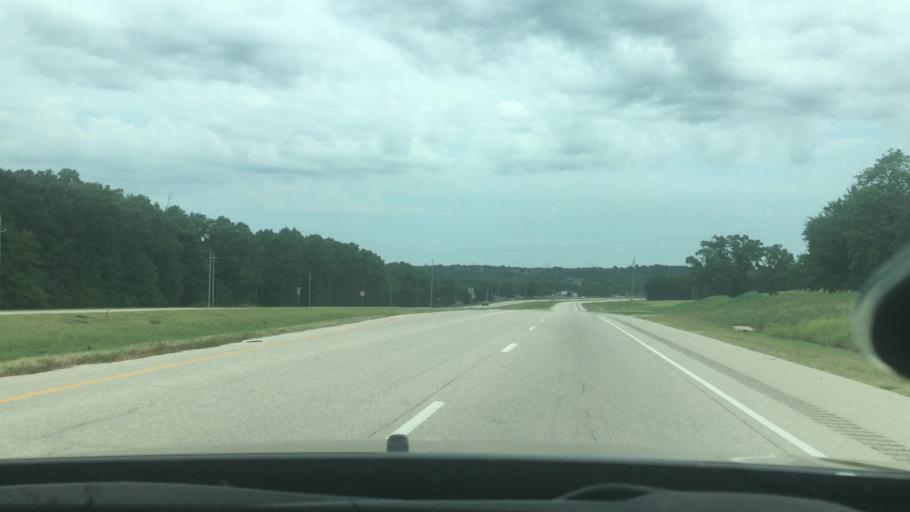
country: US
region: Oklahoma
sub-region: Pontotoc County
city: Byng
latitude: 34.9183
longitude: -96.6817
